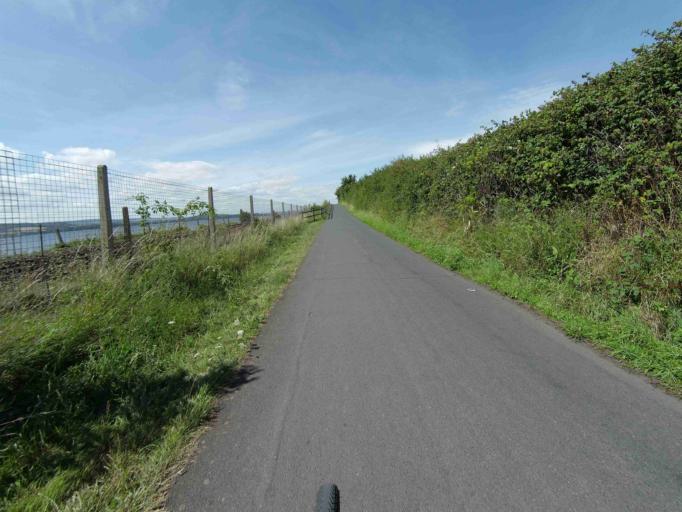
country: GB
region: England
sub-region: Devon
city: Exmouth
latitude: 50.6326
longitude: -3.4179
